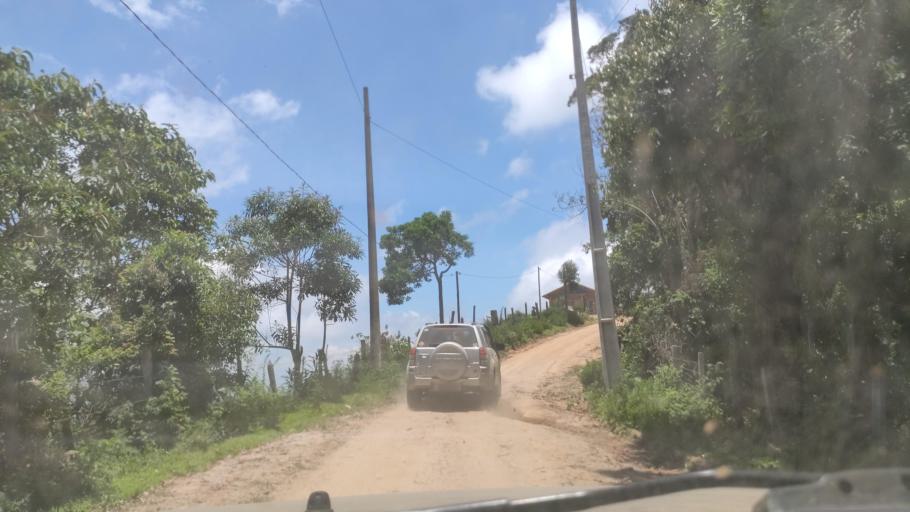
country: BR
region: Minas Gerais
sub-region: Cambui
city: Cambui
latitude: -22.6817
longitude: -45.9645
